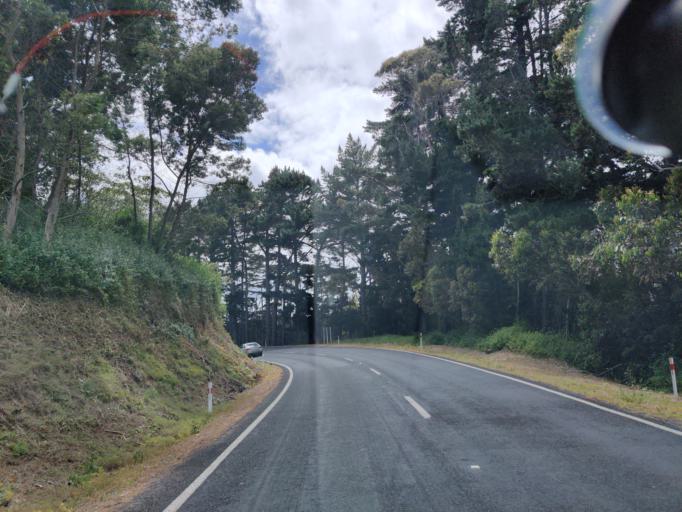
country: NZ
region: Northland
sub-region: Far North District
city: Kaitaia
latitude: -34.9511
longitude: 173.1868
